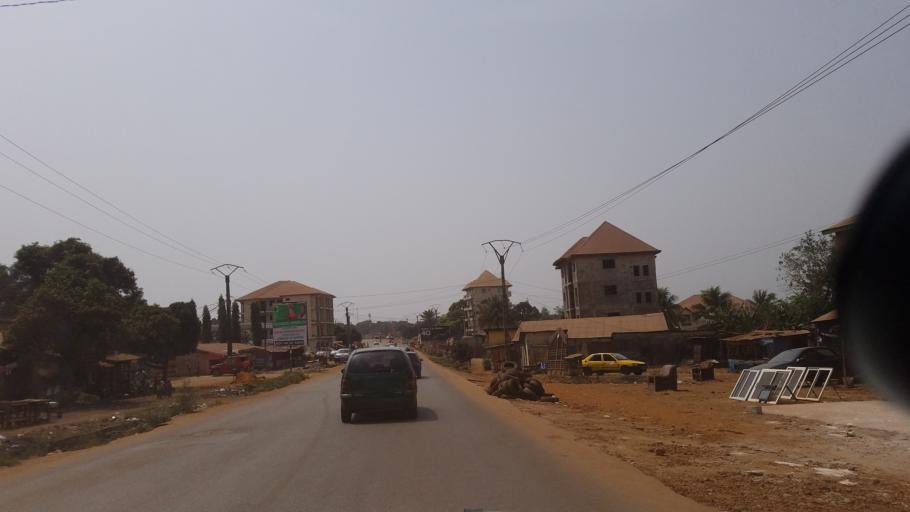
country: GN
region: Kindia
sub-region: Prefecture de Dubreka
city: Dubreka
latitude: 9.6807
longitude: -13.5740
